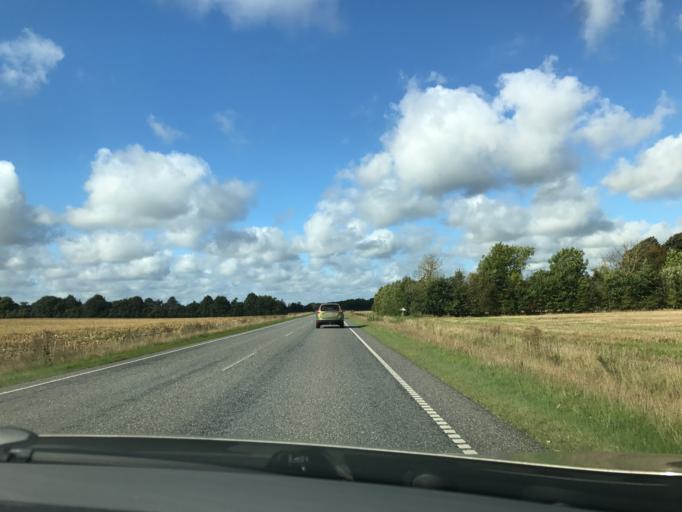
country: DK
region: South Denmark
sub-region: Billund Kommune
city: Billund
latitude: 55.7152
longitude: 9.1922
